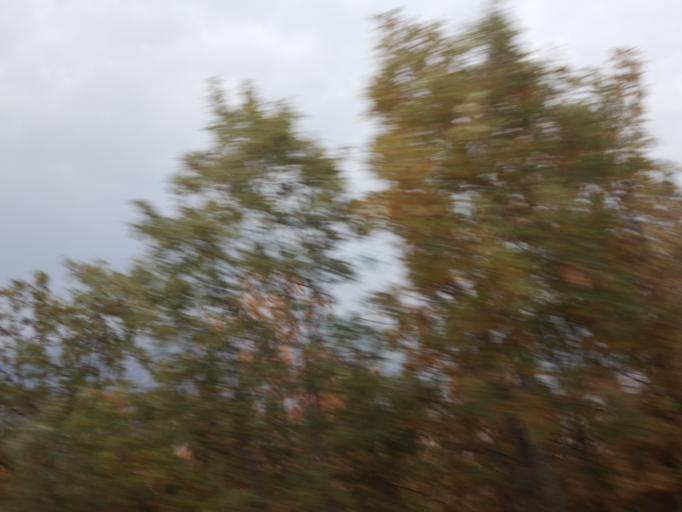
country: TR
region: Corum
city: Cemilbey
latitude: 40.3042
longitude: 35.0757
